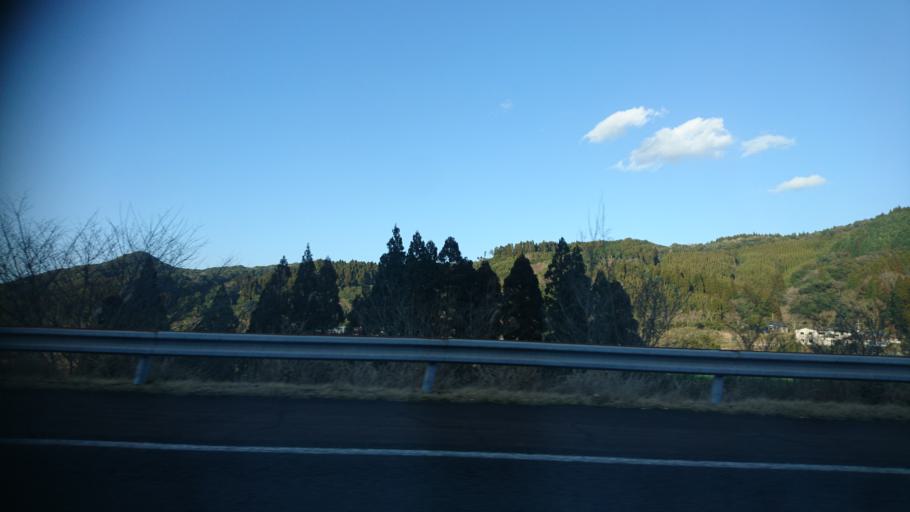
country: JP
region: Miyazaki
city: Miyakonojo
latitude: 31.7938
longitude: 131.1764
